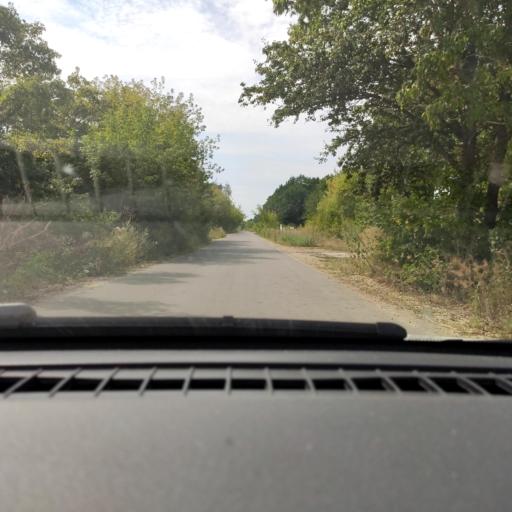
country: RU
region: Voronezj
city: Pridonskoy
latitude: 51.7387
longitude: 39.0675
